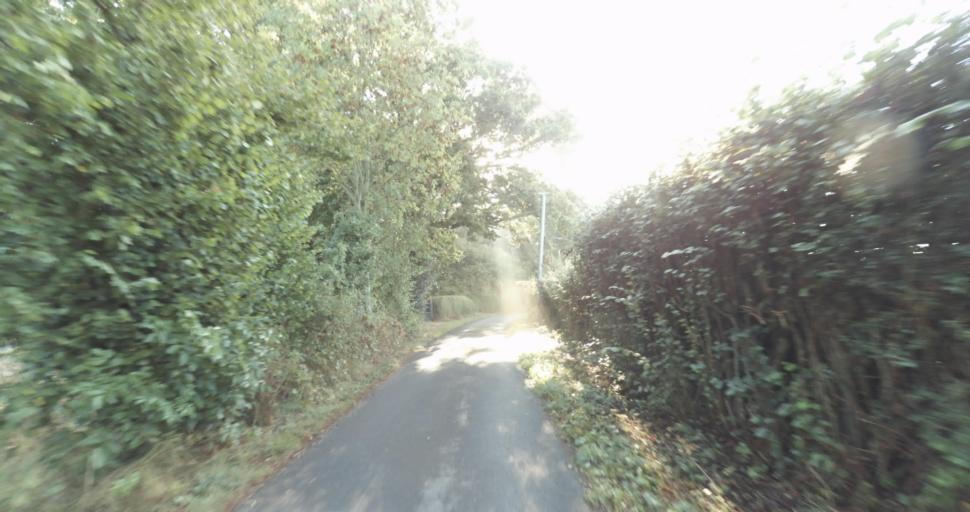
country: FR
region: Lower Normandy
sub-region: Departement de l'Orne
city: Vimoutiers
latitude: 48.9114
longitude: 0.1604
